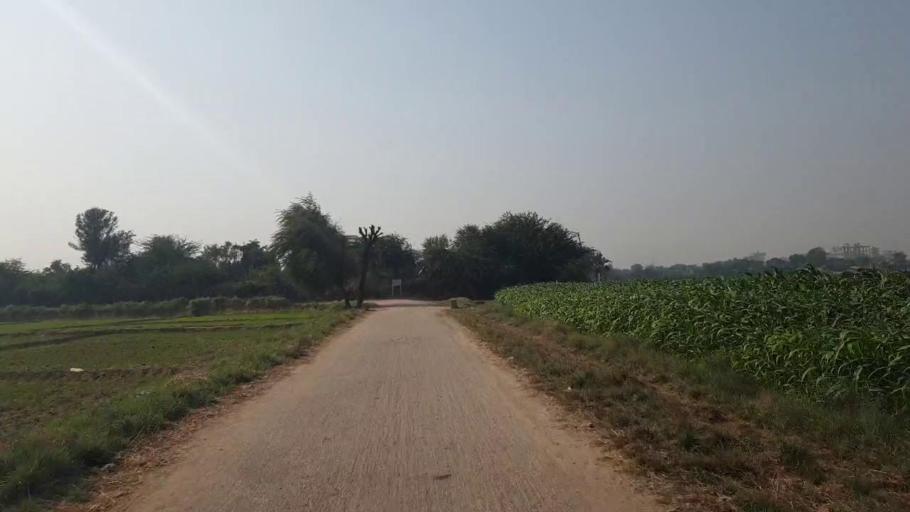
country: PK
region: Sindh
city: Kotri
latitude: 25.3527
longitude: 68.3086
